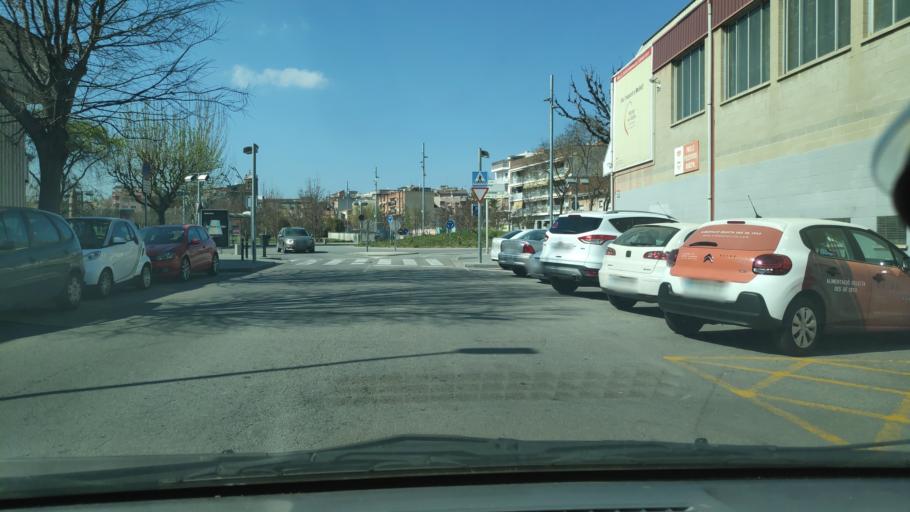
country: ES
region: Catalonia
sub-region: Provincia de Barcelona
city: Mollet del Valles
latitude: 41.5376
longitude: 2.2172
